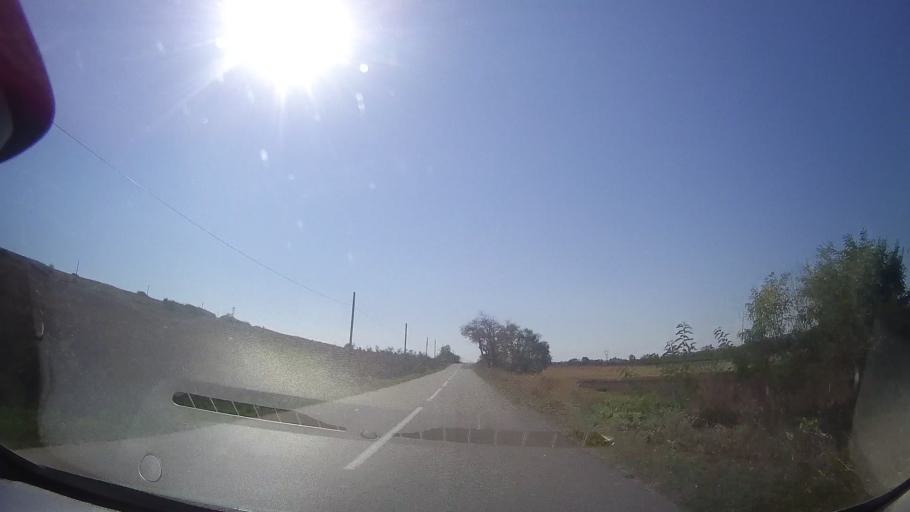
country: RO
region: Timis
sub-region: Comuna Bethausen
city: Bethausen
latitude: 45.8500
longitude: 21.9639
